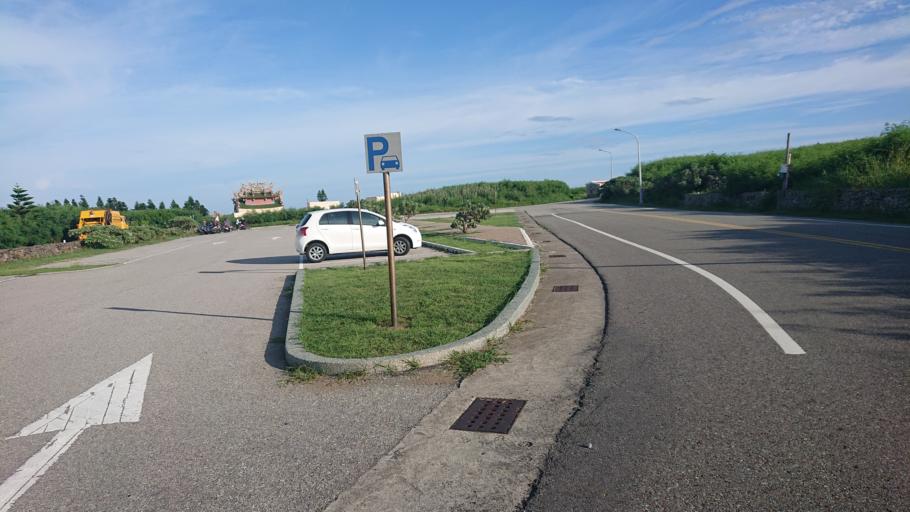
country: TW
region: Taiwan
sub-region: Penghu
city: Ma-kung
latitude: 23.6072
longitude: 119.5183
